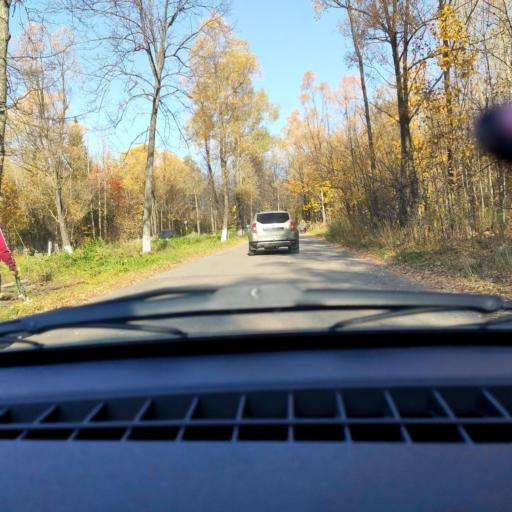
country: RU
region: Bashkortostan
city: Mikhaylovka
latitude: 54.8109
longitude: 55.8632
